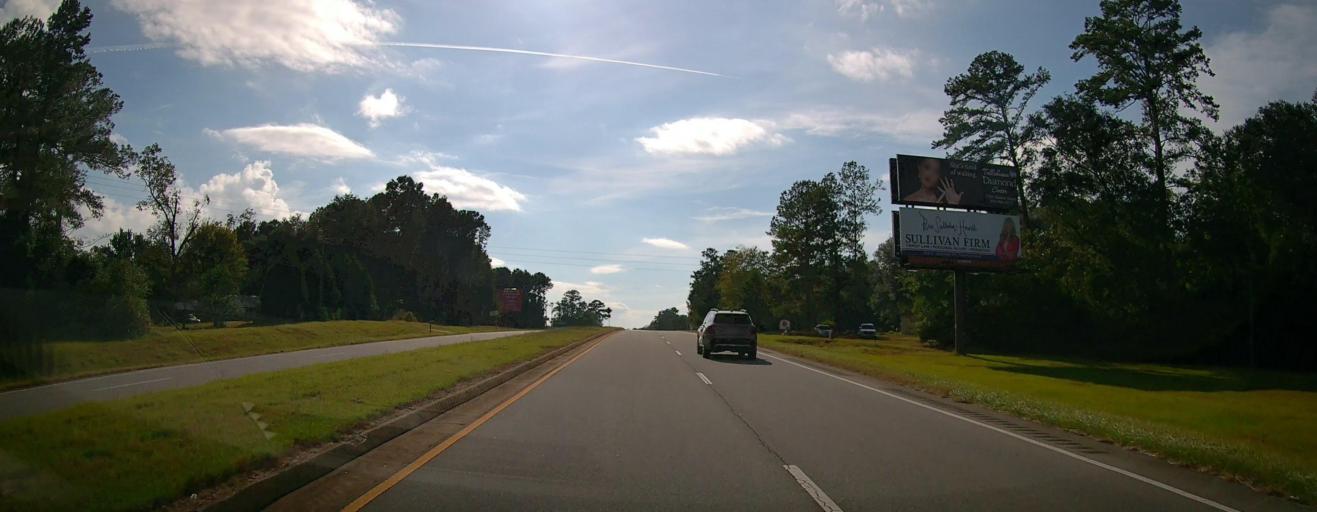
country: US
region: Georgia
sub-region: Grady County
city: Cairo
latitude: 30.7144
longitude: -84.1352
